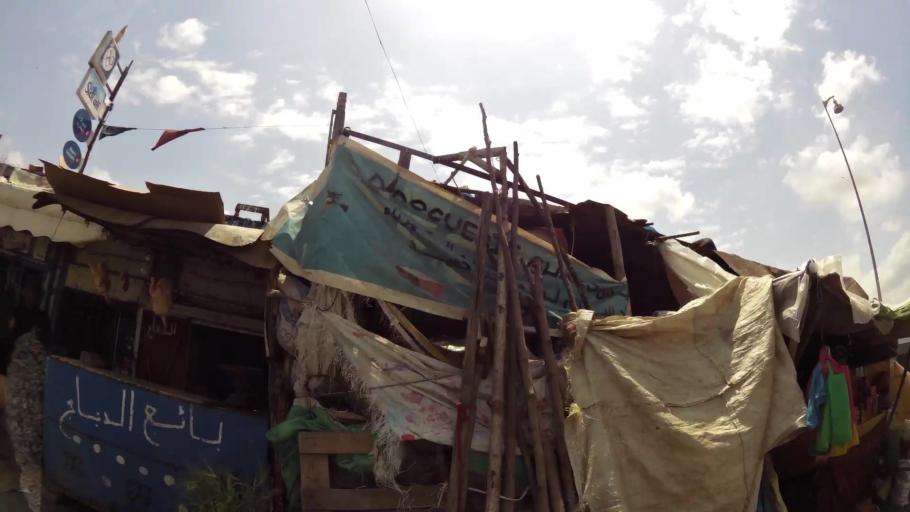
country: MA
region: Rabat-Sale-Zemmour-Zaer
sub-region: Khemisset
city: Tiflet
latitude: 34.0108
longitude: -6.5300
